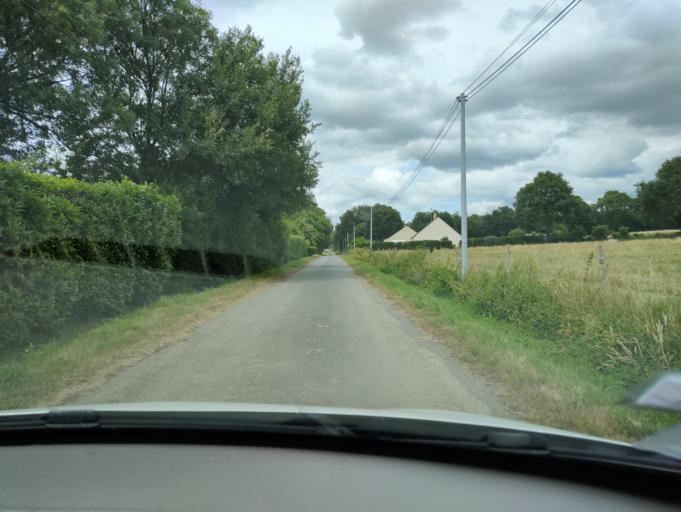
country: FR
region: Pays de la Loire
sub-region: Departement de la Loire-Atlantique
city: Chateaubriant
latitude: 47.7032
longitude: -1.4258
